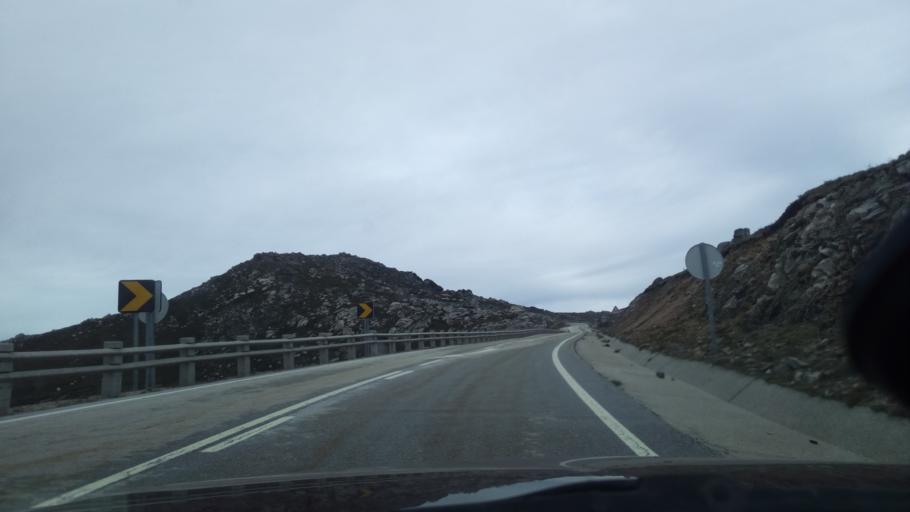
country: PT
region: Guarda
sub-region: Seia
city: Seia
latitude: 40.3505
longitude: -7.6876
